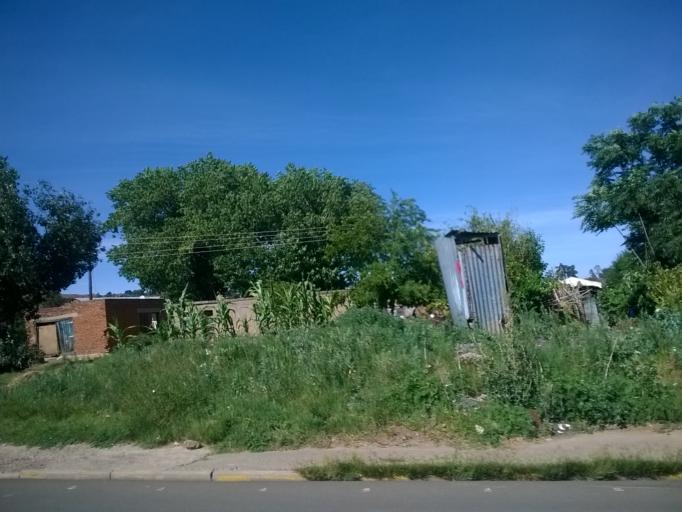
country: LS
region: Maseru
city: Maseru
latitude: -29.3081
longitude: 27.4985
